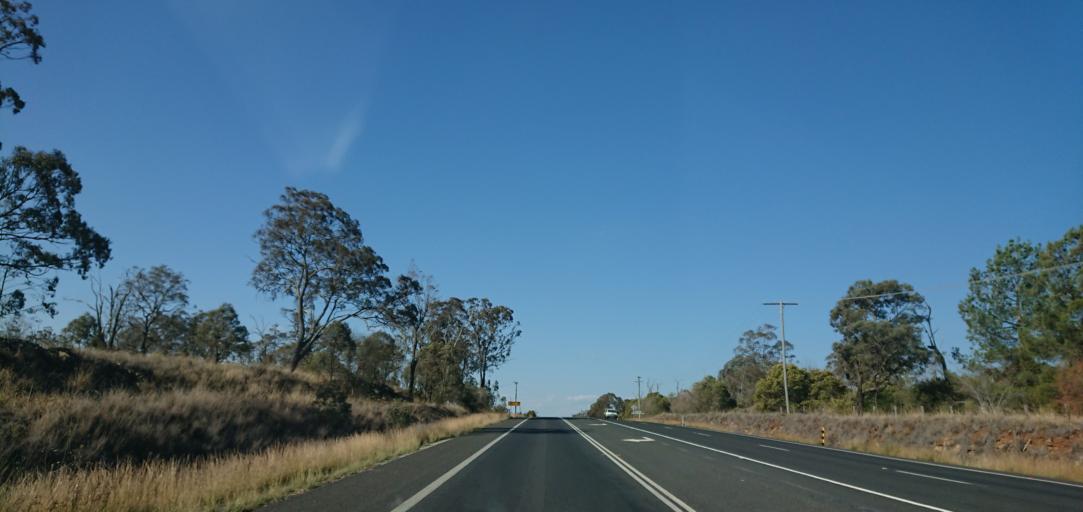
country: AU
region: Queensland
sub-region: Toowoomba
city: Westbrook
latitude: -27.6269
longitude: 151.7577
